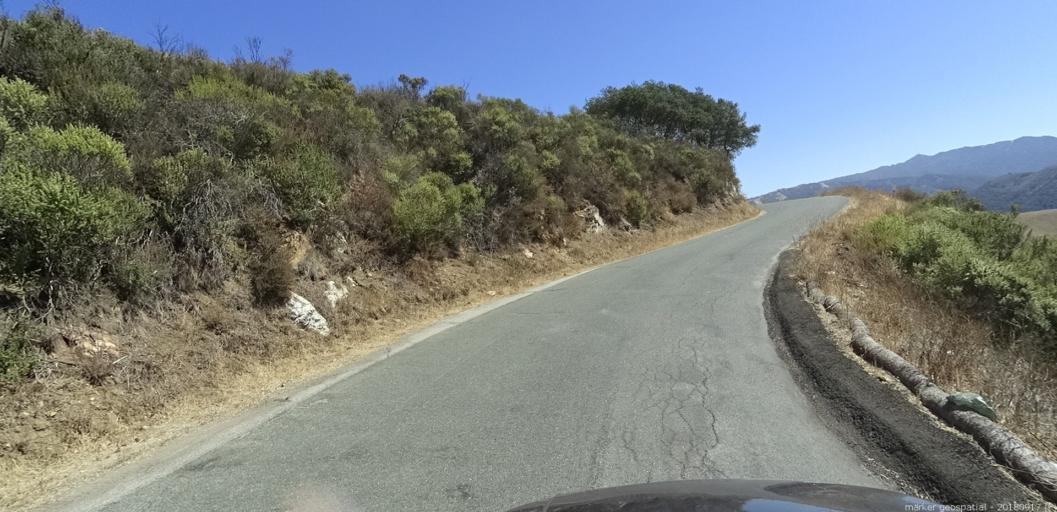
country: US
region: California
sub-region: San Benito County
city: San Juan Bautista
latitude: 36.8127
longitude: -121.5764
